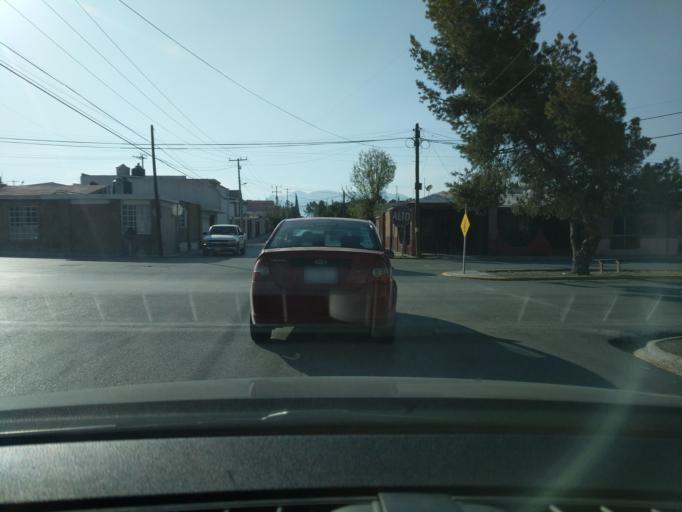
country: MX
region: Coahuila
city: Saltillo
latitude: 25.4635
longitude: -100.9870
